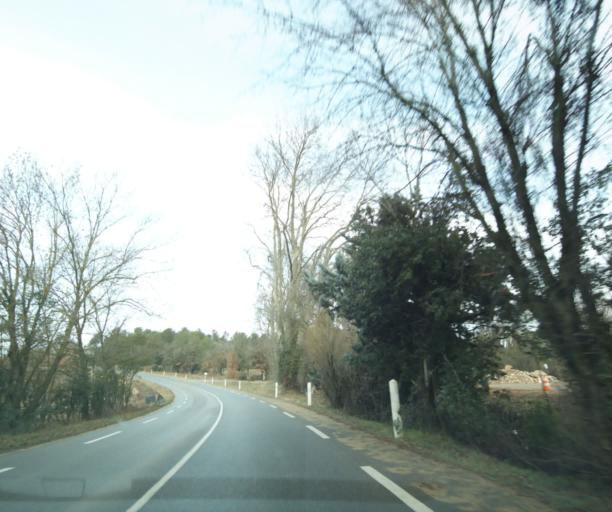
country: FR
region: Provence-Alpes-Cote d'Azur
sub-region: Departement du Var
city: Tourves
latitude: 43.3945
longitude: 5.9742
